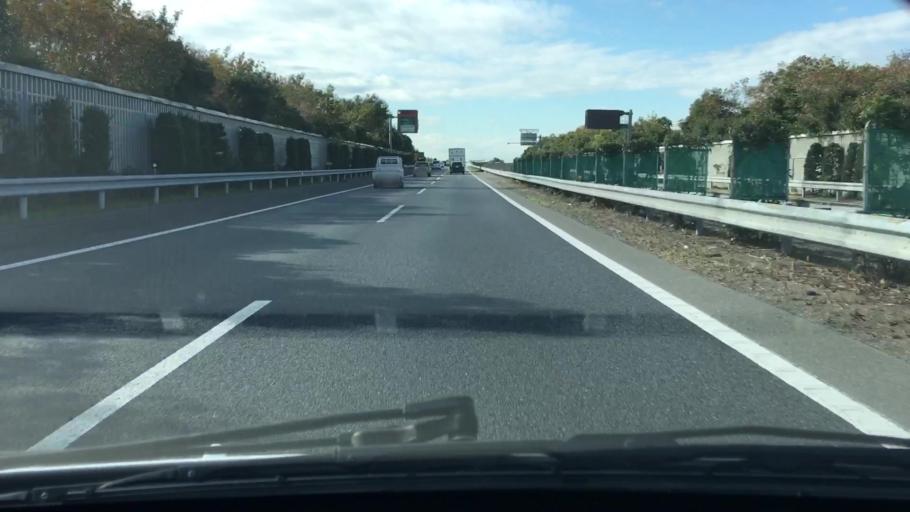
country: JP
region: Chiba
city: Ichihara
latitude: 35.4932
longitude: 140.0901
